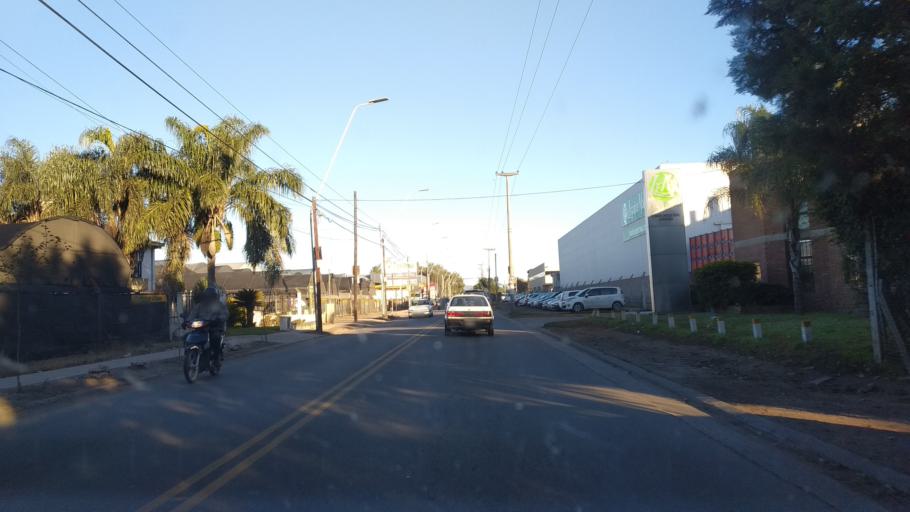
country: AR
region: Cordoba
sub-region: Departamento de Capital
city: Cordoba
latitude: -31.3432
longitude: -64.2100
